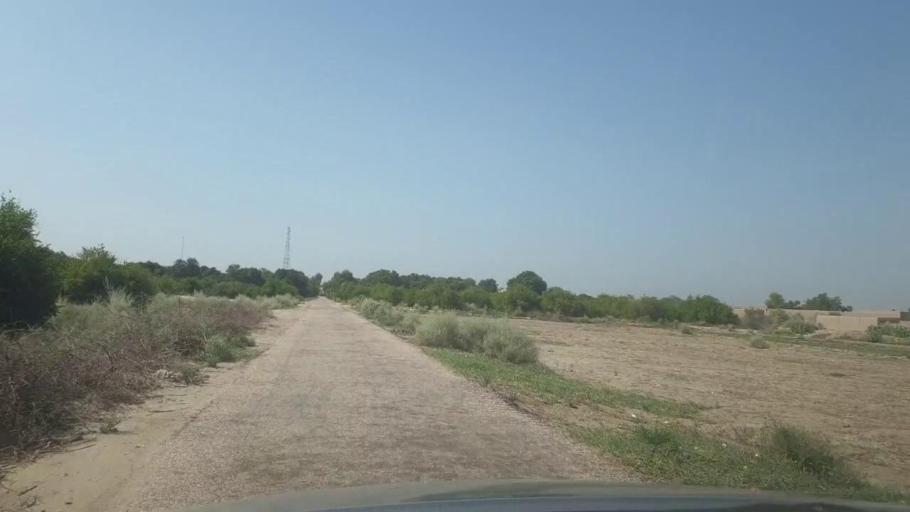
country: PK
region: Sindh
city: Rohri
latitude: 27.4101
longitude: 69.0805
